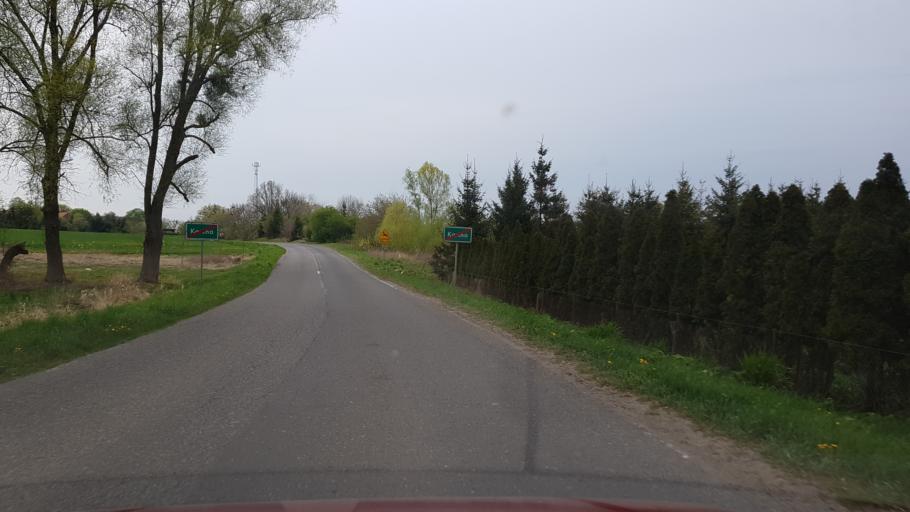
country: PL
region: West Pomeranian Voivodeship
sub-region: Powiat pyrzycki
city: Bielice
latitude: 53.2721
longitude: 14.6817
